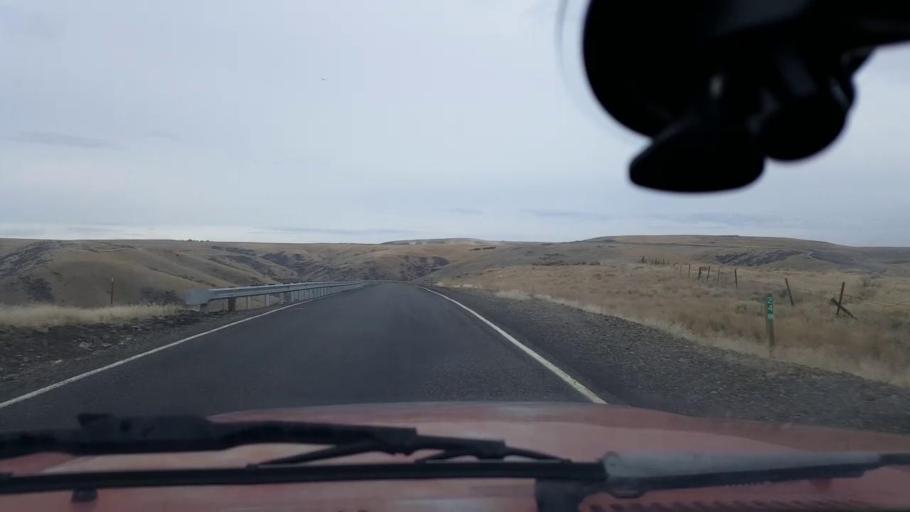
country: US
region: Washington
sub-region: Asotin County
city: Clarkston Heights-Vineland
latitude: 46.3329
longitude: -117.2916
